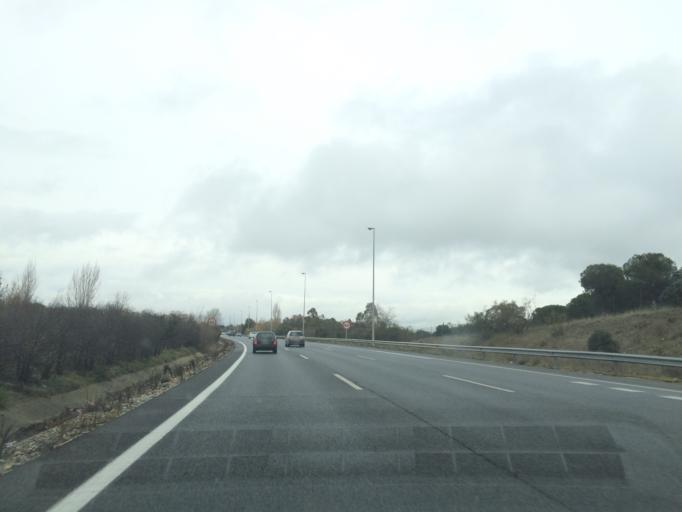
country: ES
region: Madrid
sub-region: Provincia de Madrid
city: Tres Cantos
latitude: 40.5651
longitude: -3.7102
